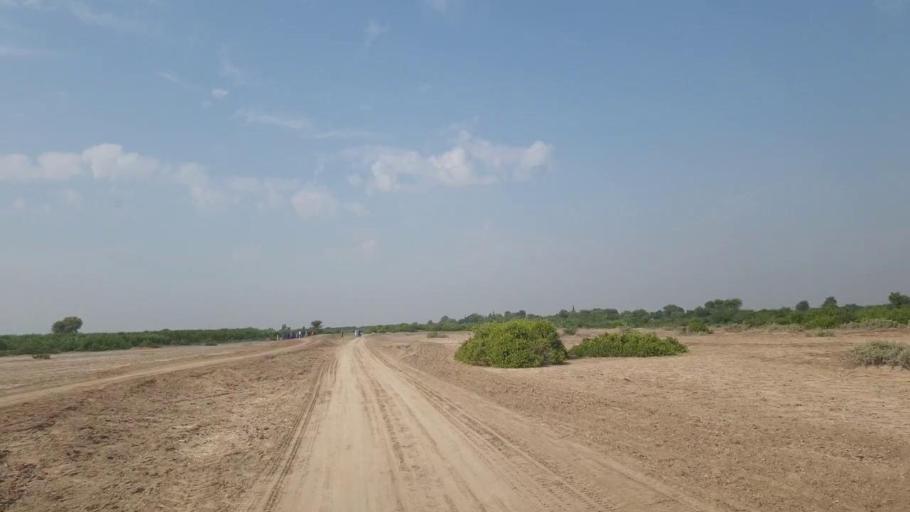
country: PK
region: Sindh
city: Digri
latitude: 25.0320
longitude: 69.0700
